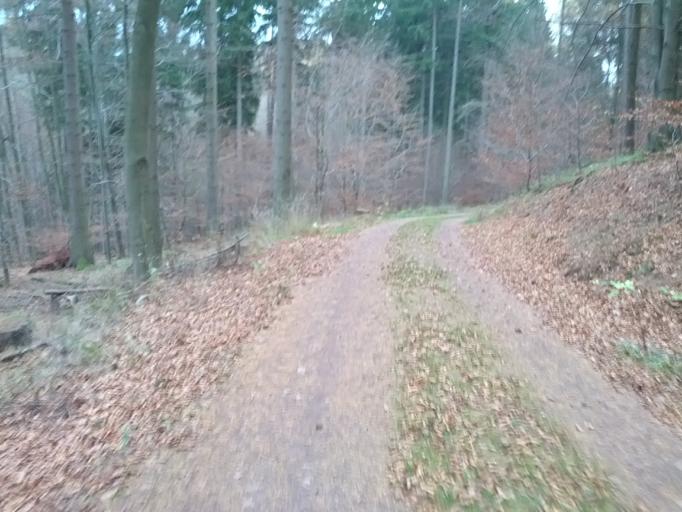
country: DE
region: Thuringia
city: Eisenach
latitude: 50.9420
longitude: 10.3095
